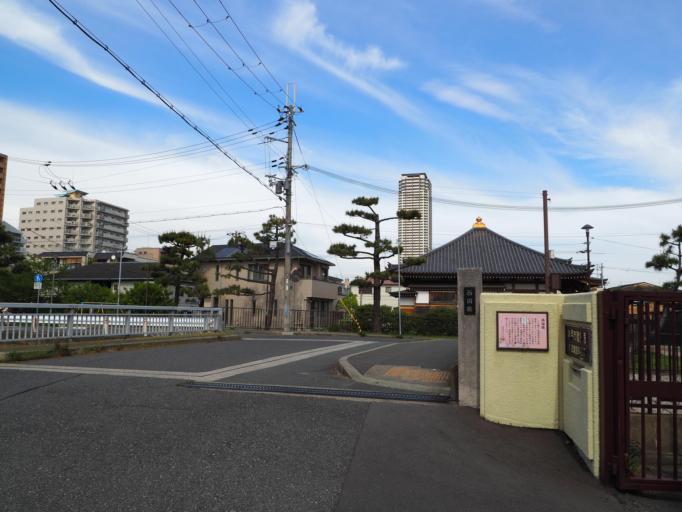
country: JP
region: Hyogo
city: Ashiya
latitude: 34.7141
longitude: 135.2494
